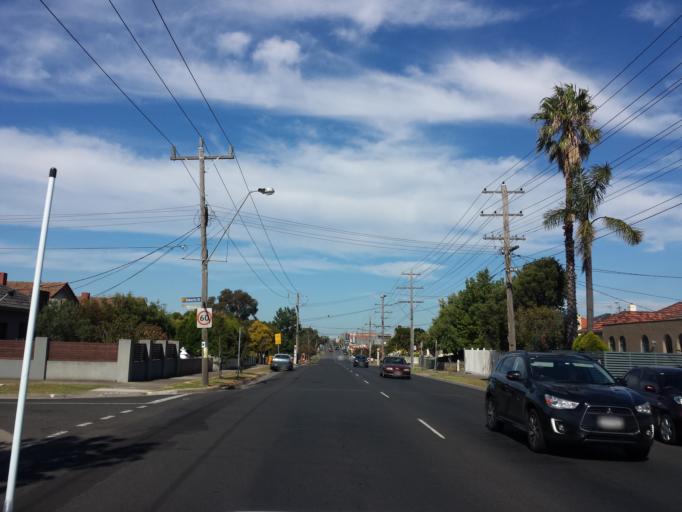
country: AU
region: Victoria
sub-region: Moonee Valley
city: Essendon North
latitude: -37.7548
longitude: 144.8979
